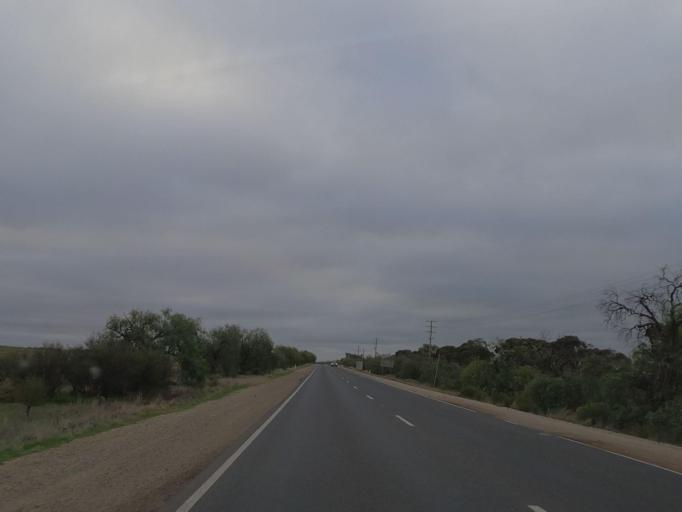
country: AU
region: Victoria
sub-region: Swan Hill
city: Swan Hill
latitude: -35.4489
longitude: 143.6228
